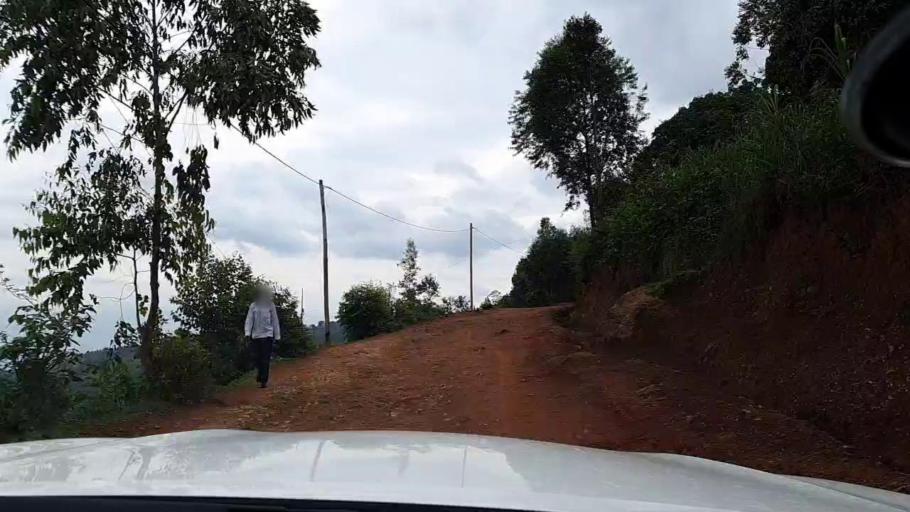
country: RW
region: Western Province
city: Kibuye
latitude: -2.1878
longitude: 29.2973
